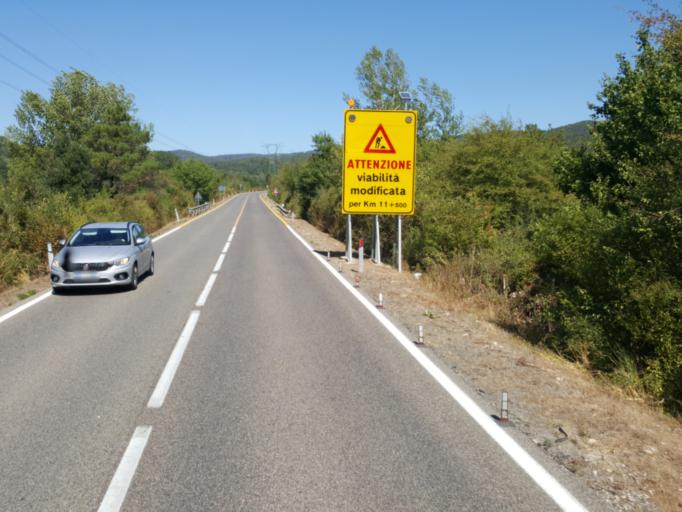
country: IT
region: Tuscany
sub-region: Provincia di Grosseto
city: Civitella Marittima
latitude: 43.0197
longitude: 11.2835
